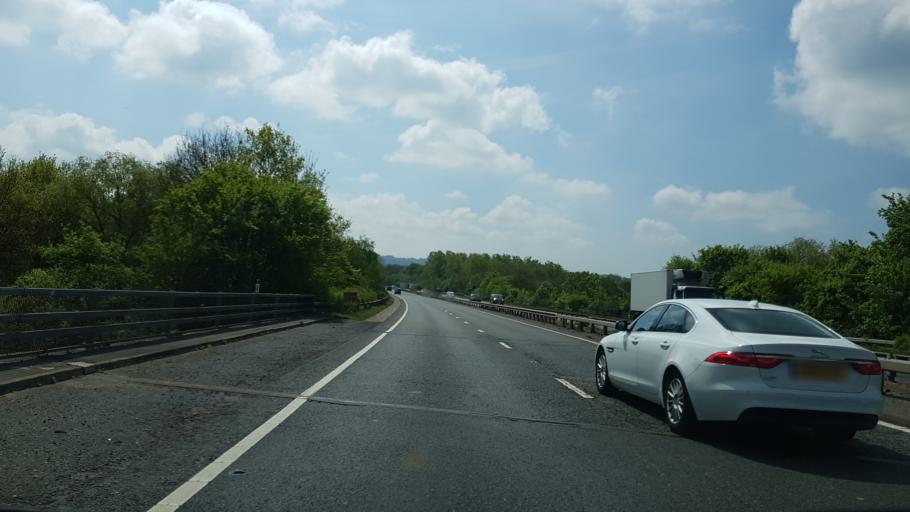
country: GB
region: England
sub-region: Kent
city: Tonbridge
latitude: 51.2117
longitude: 0.2254
